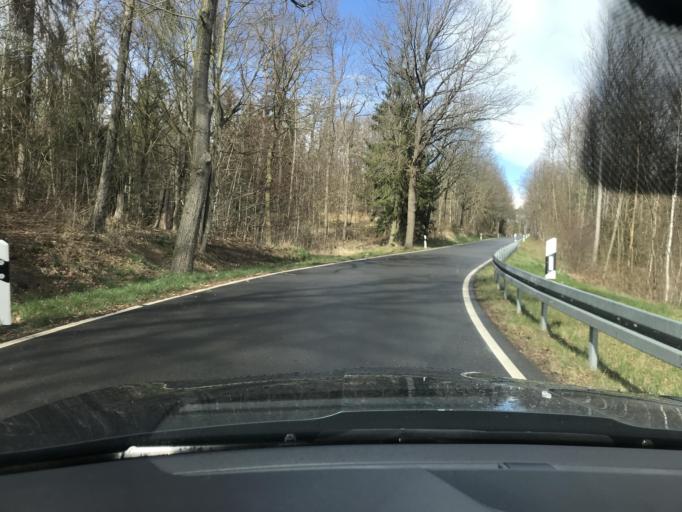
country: DE
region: Saxony-Anhalt
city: Hoym
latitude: 51.6972
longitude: 11.3222
